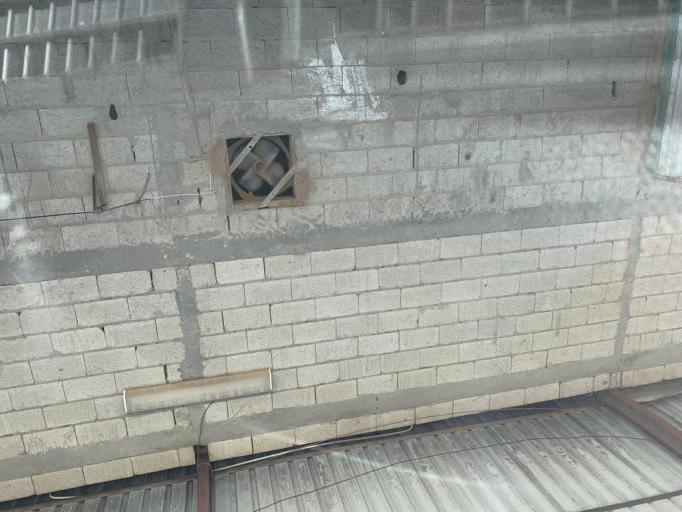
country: BH
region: Manama
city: Jidd Hafs
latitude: 26.2267
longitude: 50.4928
